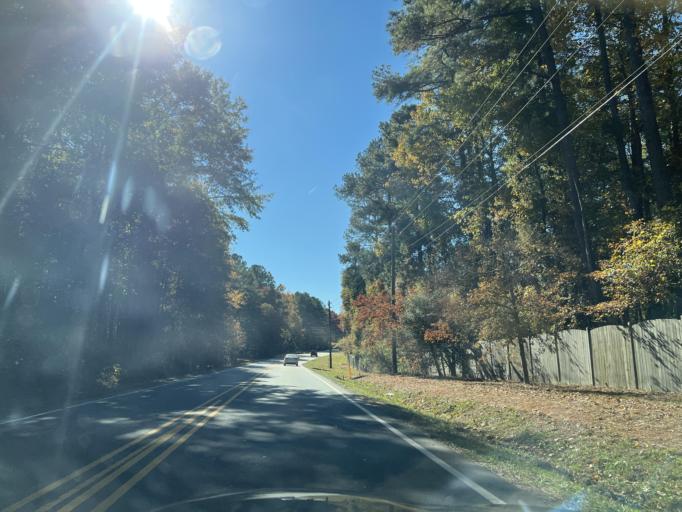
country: US
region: North Carolina
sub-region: Wake County
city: Garner
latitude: 35.7136
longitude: -78.6859
